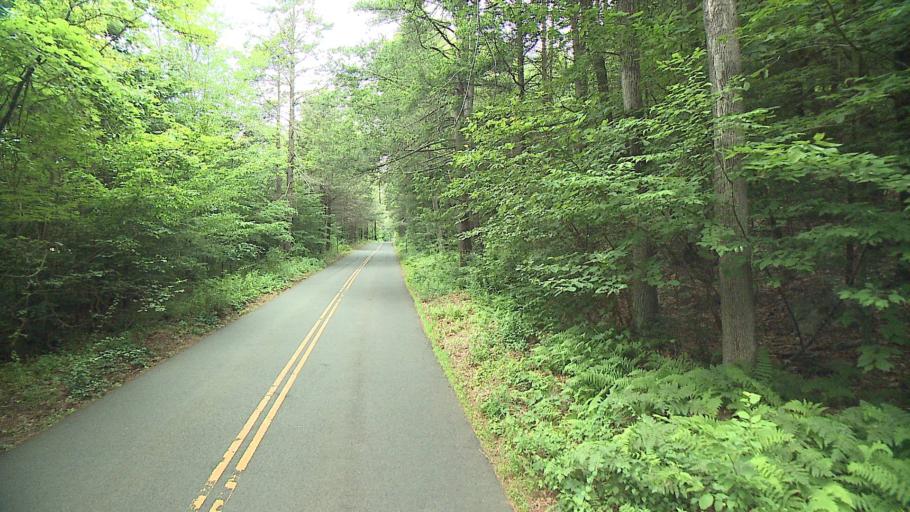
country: US
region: Connecticut
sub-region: Litchfield County
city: New Hartford Center
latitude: 41.9275
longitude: -72.9999
